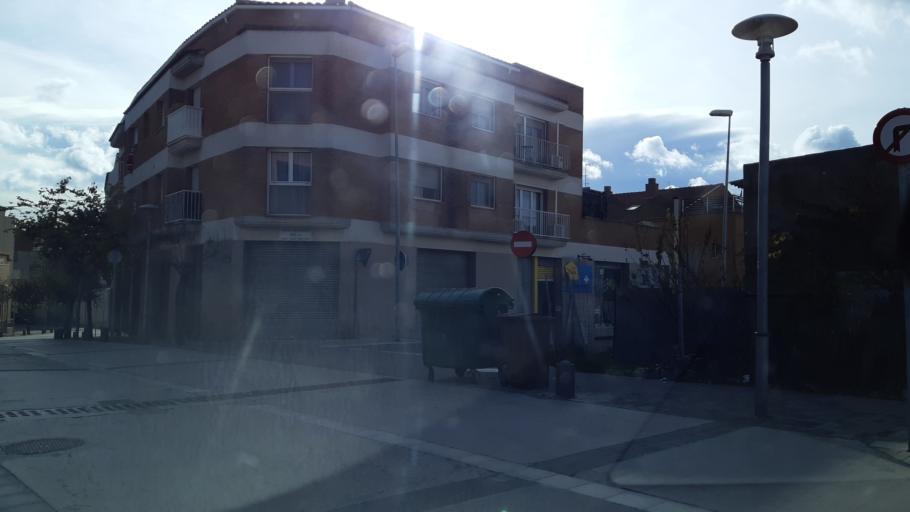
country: ES
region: Catalonia
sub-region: Provincia de Barcelona
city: Vilanova del Cami
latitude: 41.5711
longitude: 1.6355
